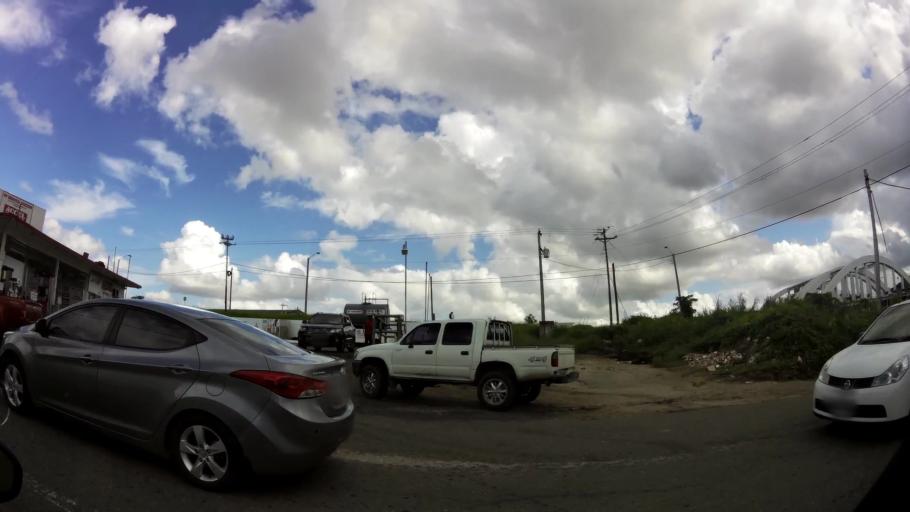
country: TT
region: City of San Fernando
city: Mon Repos
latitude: 10.2632
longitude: -61.4587
